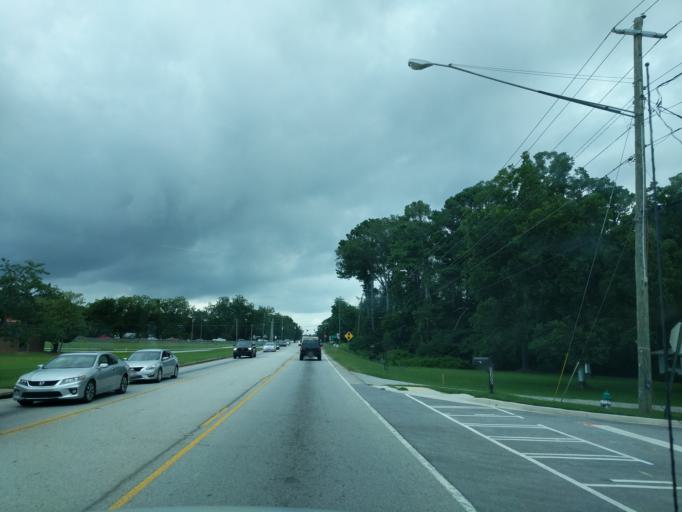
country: US
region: Georgia
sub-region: Walton County
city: Loganville
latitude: 33.8424
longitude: -83.8967
